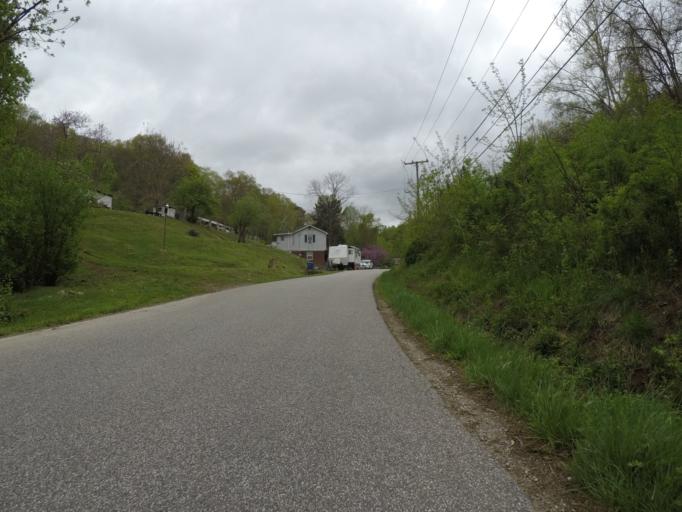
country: US
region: West Virginia
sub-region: Cabell County
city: Barboursville
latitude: 38.4065
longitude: -82.2840
